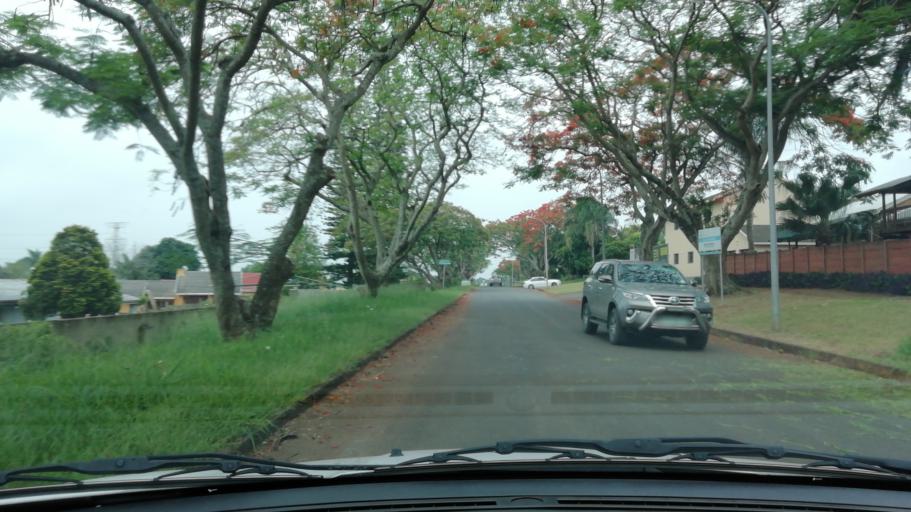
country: ZA
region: KwaZulu-Natal
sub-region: uThungulu District Municipality
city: Empangeni
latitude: -28.7392
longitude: 31.8887
